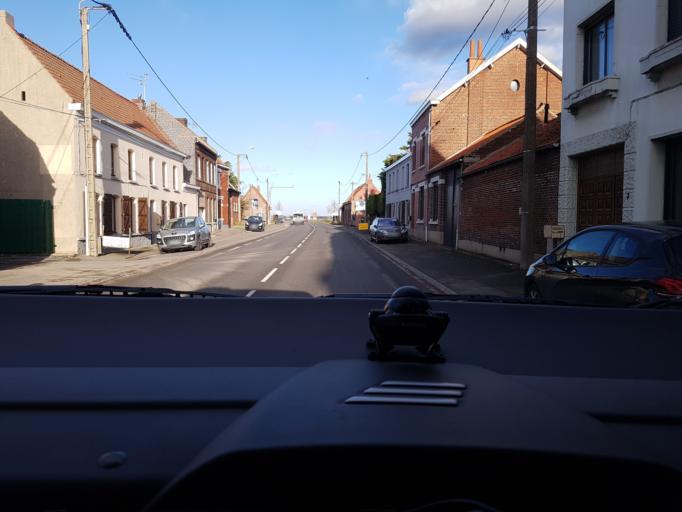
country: FR
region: Nord-Pas-de-Calais
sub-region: Departement du Nord
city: Camphin-en-Carembault
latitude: 50.5145
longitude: 2.9861
